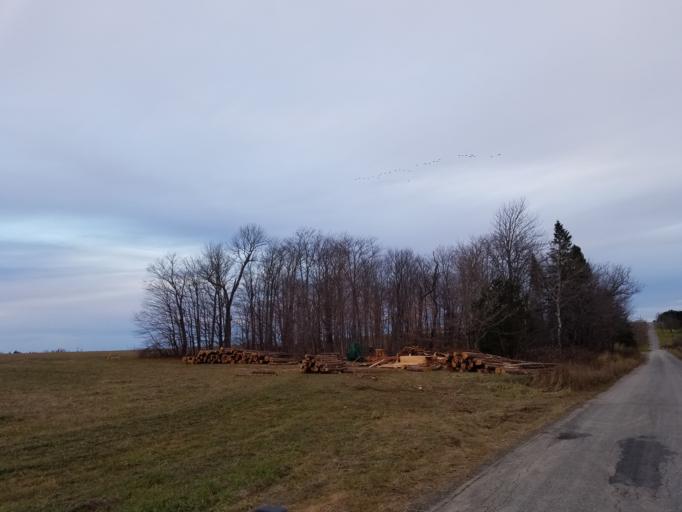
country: US
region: Maine
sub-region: Aroostook County
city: Caribou
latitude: 46.8672
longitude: -68.2042
